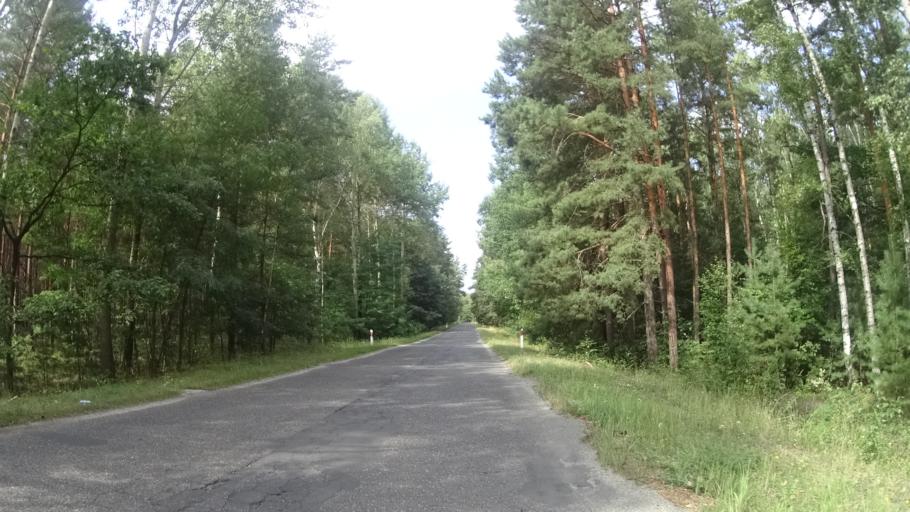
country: PL
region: Lubusz
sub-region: Powiat zarski
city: Leknica
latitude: 51.5418
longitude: 14.7825
